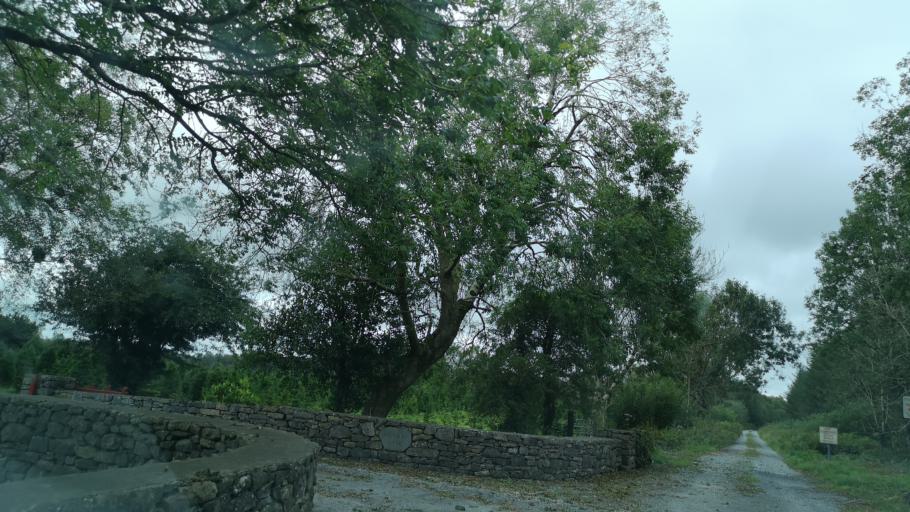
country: IE
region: Connaught
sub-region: County Galway
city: Athenry
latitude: 53.3000
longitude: -8.6675
